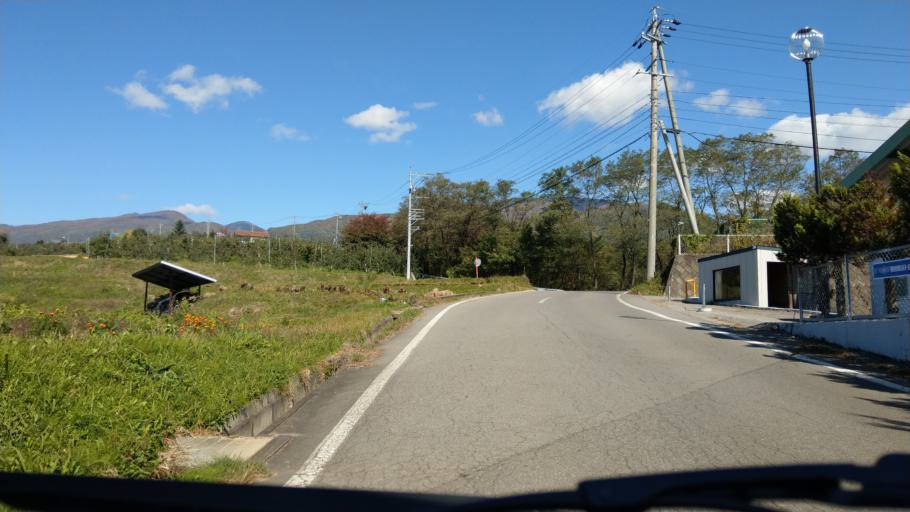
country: JP
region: Nagano
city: Komoro
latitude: 36.3539
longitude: 138.4018
